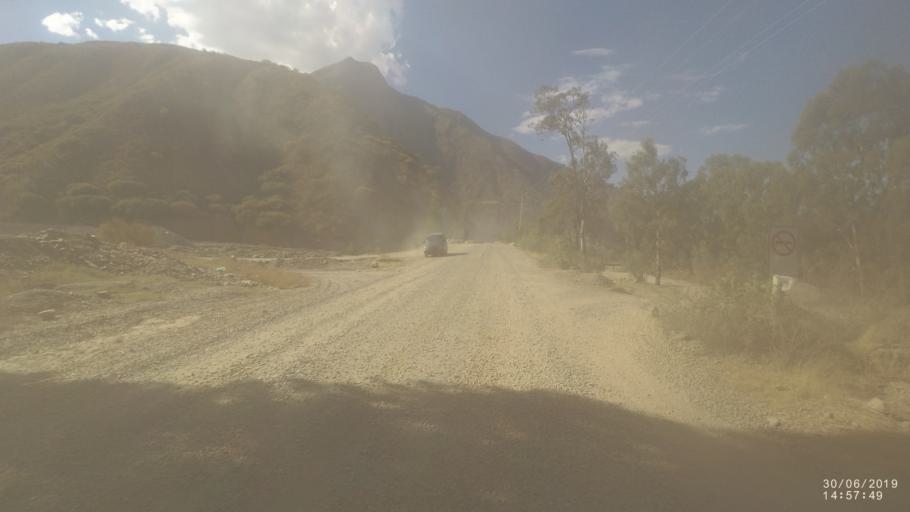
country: BO
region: Cochabamba
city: Irpa Irpa
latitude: -17.7422
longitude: -66.3522
